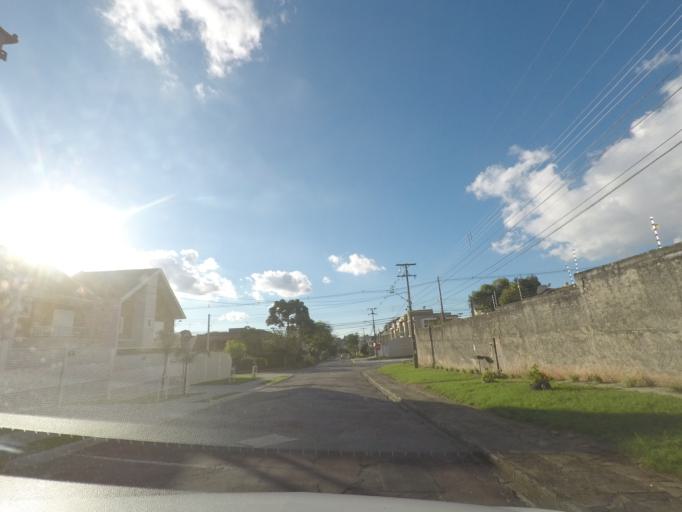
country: BR
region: Parana
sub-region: Sao Jose Dos Pinhais
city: Sao Jose dos Pinhais
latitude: -25.4972
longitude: -49.2536
